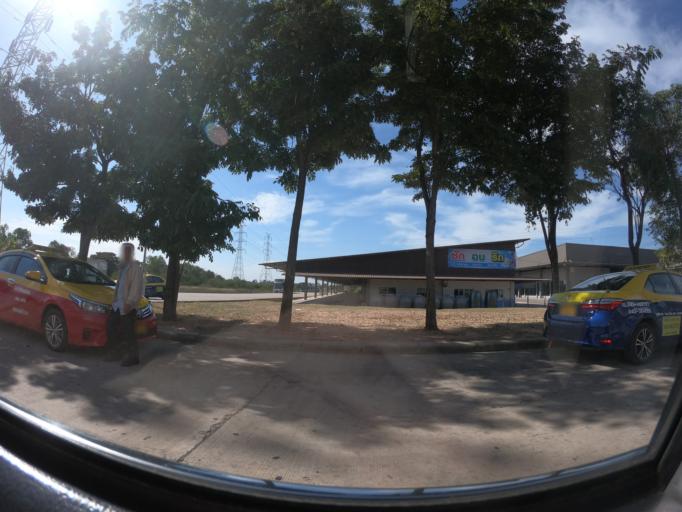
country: TH
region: Khon Kaen
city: Khon Kaen
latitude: 16.3889
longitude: 102.8052
